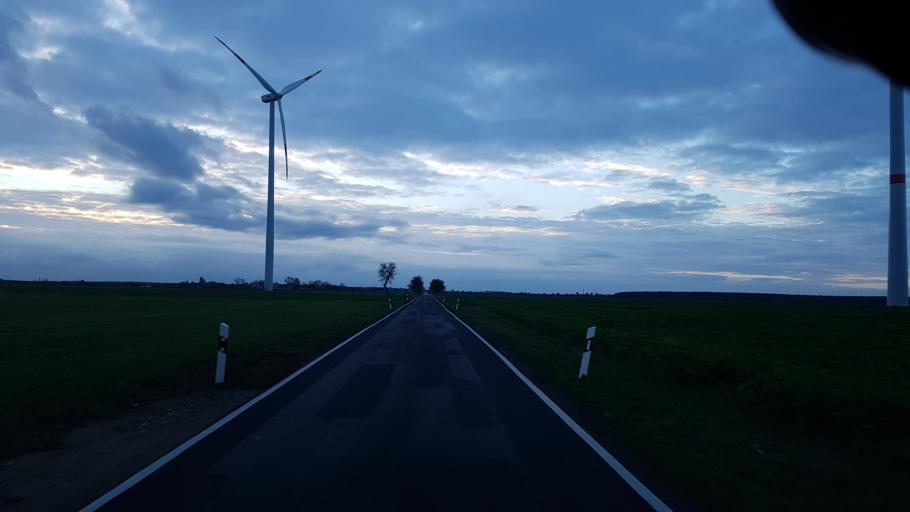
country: DE
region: Brandenburg
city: Muhlberg
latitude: 51.4688
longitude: 13.2449
